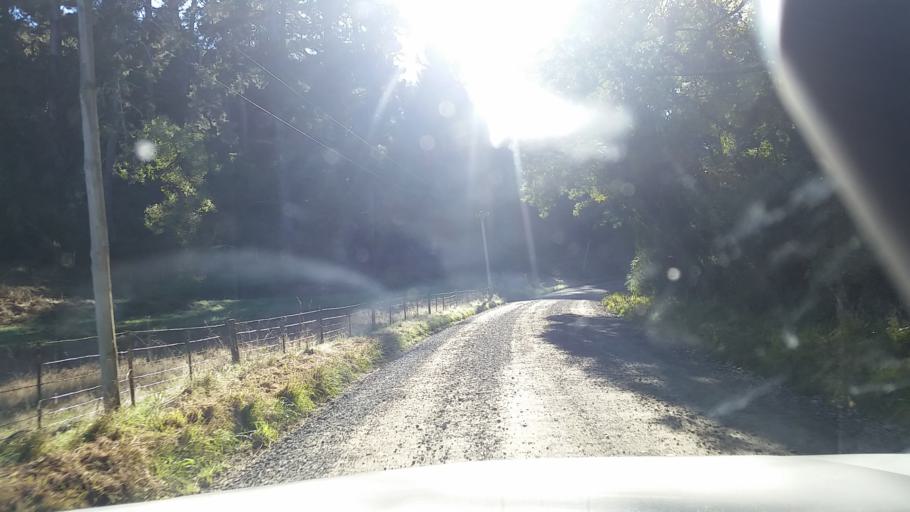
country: NZ
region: Marlborough
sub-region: Marlborough District
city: Blenheim
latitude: -41.4506
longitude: 173.8726
